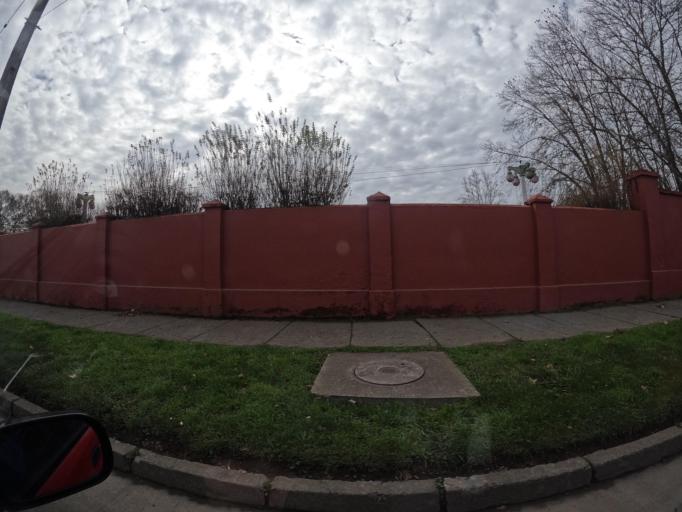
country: CL
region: Maule
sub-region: Provincia de Linares
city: Linares
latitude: -35.8407
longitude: -71.5922
